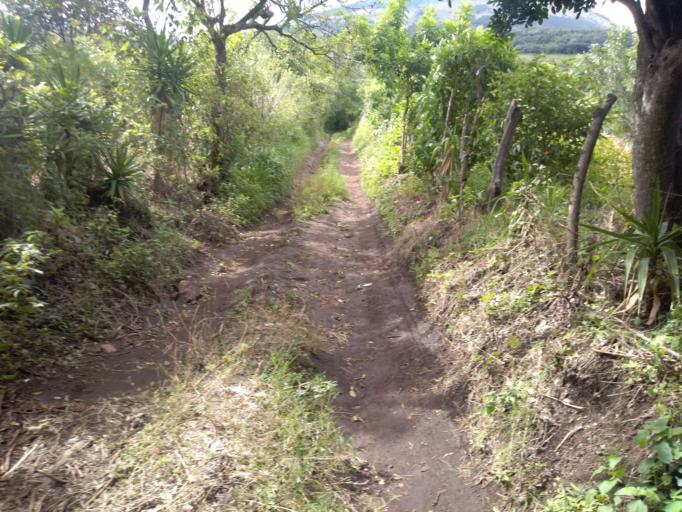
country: GT
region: Escuintla
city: San Vicente Pacaya
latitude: 14.3729
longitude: -90.5707
